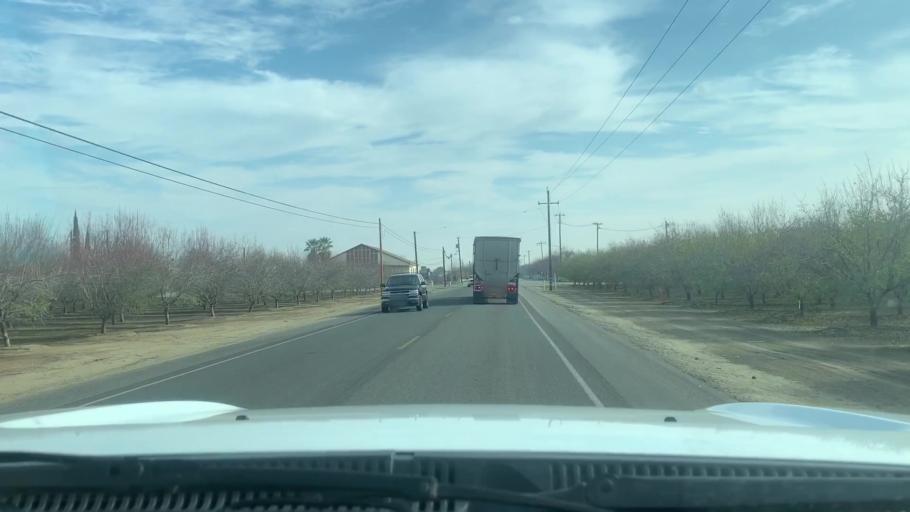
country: US
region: California
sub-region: Kern County
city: Shafter
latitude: 35.4999
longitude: -119.2977
